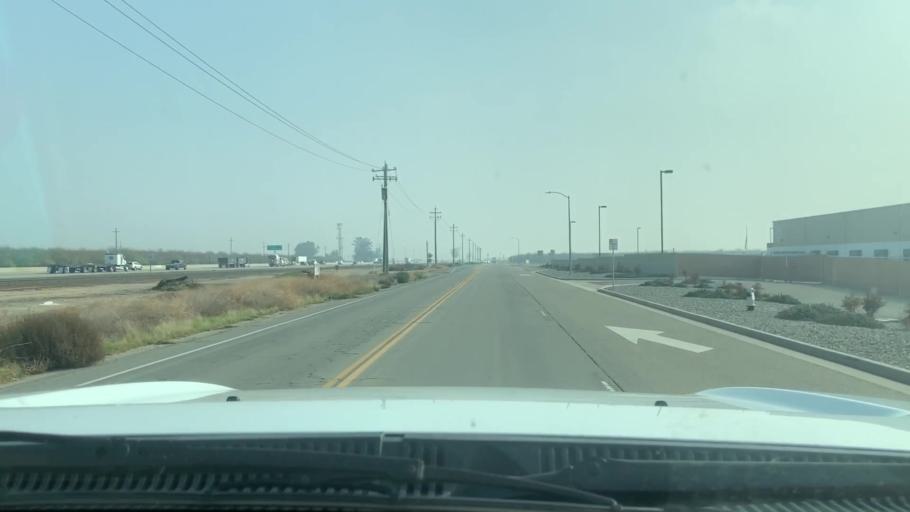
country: US
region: California
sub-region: Kern County
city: Rosedale
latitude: 35.4941
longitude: -119.1583
